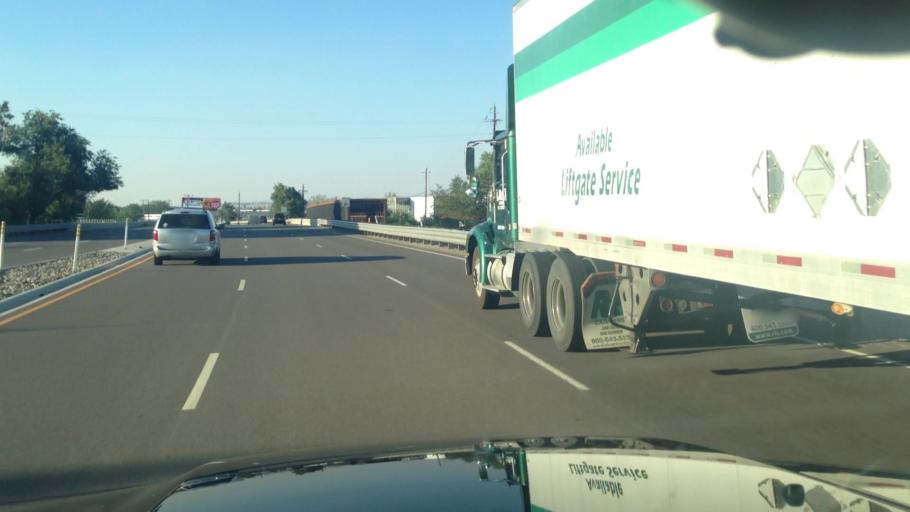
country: US
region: Nevada
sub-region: Washoe County
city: Sparks
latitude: 39.5163
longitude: -119.7414
